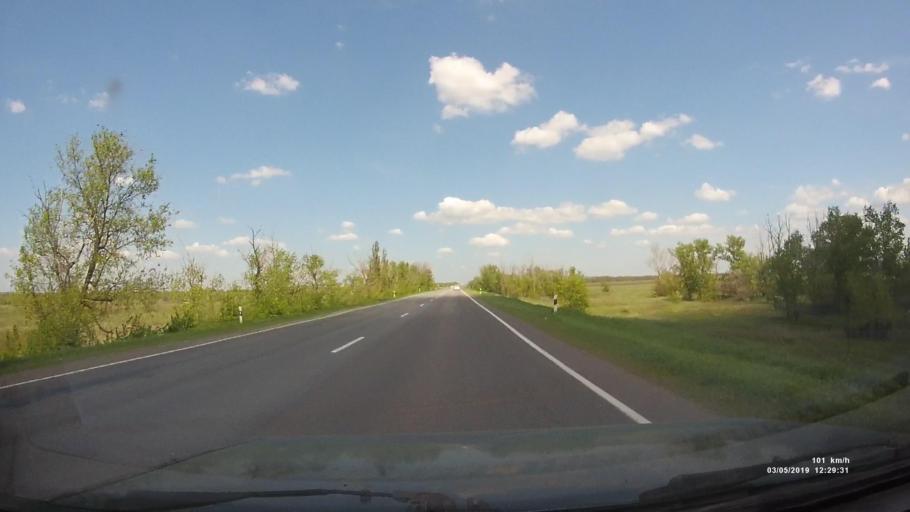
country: RU
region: Rostov
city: Semikarakorsk
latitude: 47.4888
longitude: 40.7363
